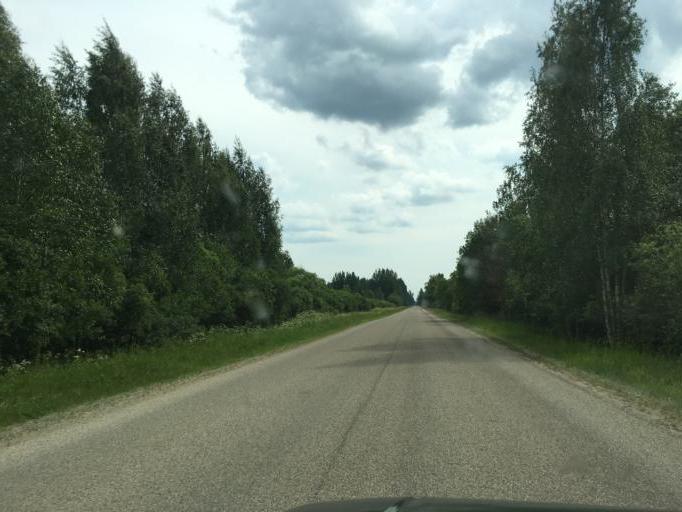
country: LV
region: Rugaju
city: Rugaji
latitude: 56.8354
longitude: 27.0934
